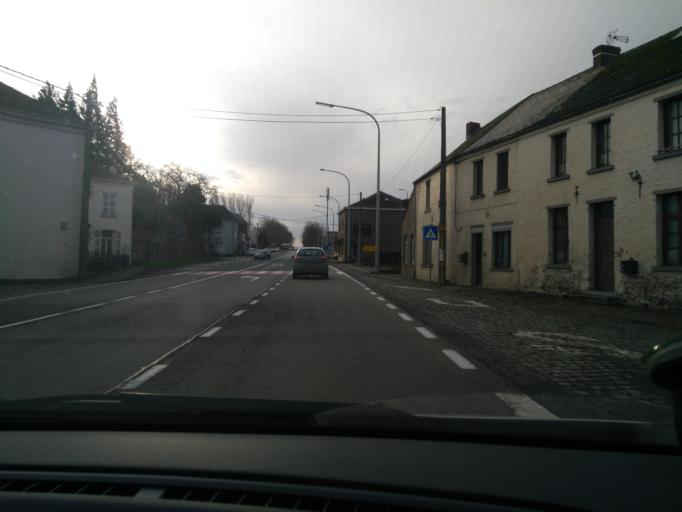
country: BE
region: Wallonia
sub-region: Province du Hainaut
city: Quevy-le-Petit
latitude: 50.3508
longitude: 3.9680
